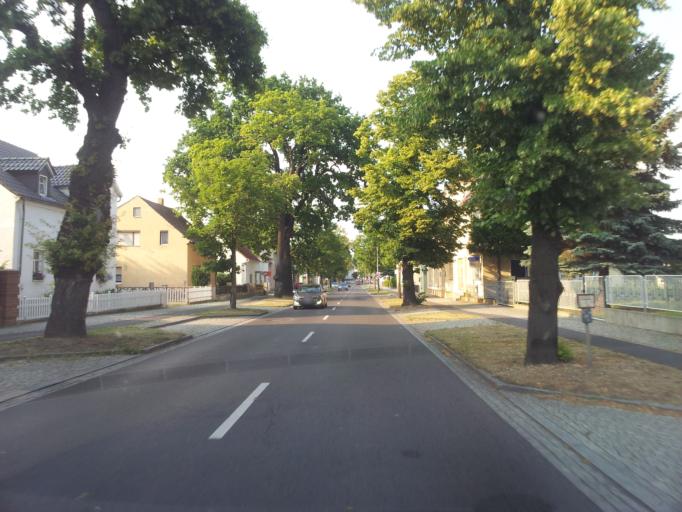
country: DE
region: Saxony
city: Bernsdorf
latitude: 51.3712
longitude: 14.0667
